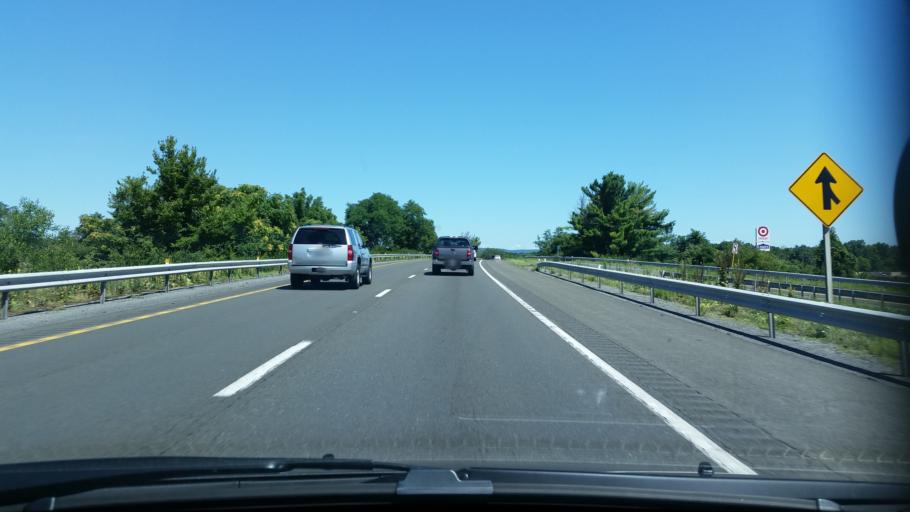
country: US
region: Virginia
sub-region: City of Winchester
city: Winchester
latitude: 39.2195
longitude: -78.1379
